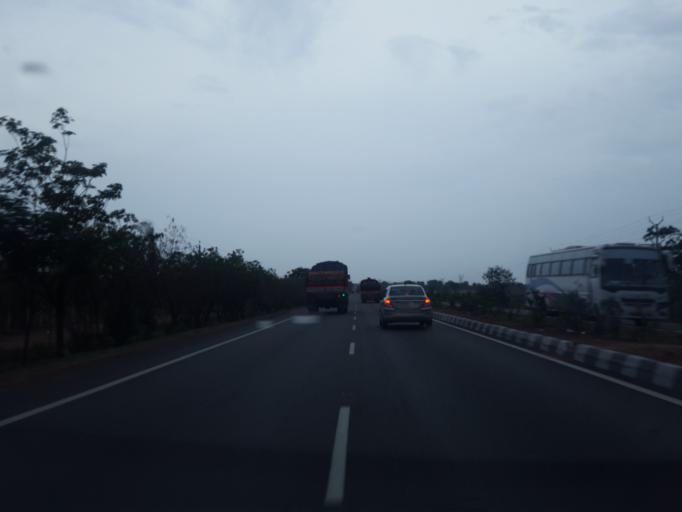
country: IN
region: Telangana
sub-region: Mahbubnagar
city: Farrukhnagar
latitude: 17.1269
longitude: 78.2777
